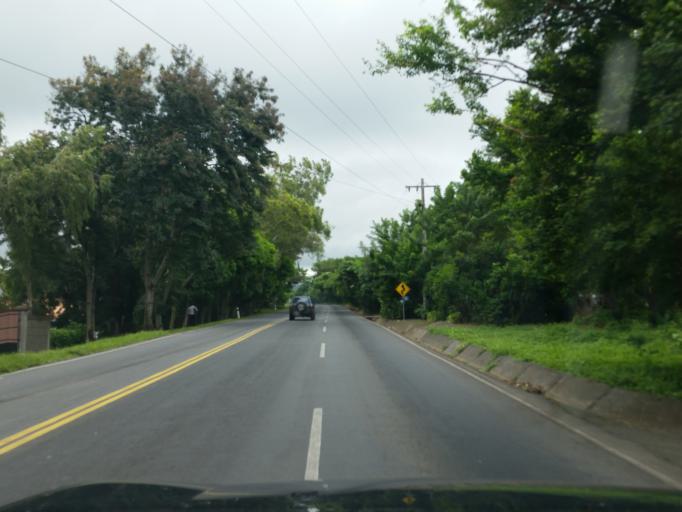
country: NI
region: Managua
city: El Crucero
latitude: 12.0524
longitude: -86.3155
